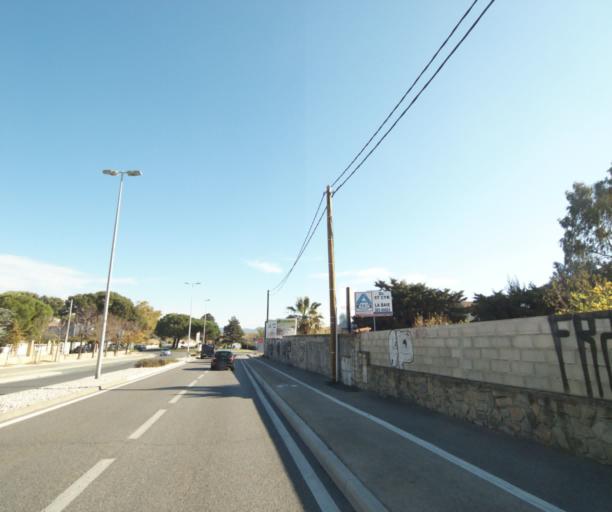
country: FR
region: Provence-Alpes-Cote d'Azur
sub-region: Departement des Bouches-du-Rhone
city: La Ciotat
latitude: 43.1920
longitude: 5.6165
